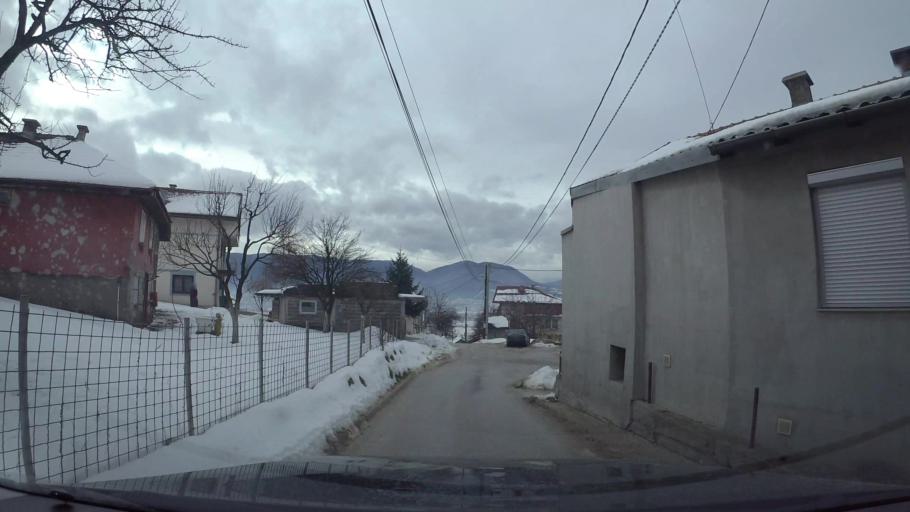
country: BA
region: Federation of Bosnia and Herzegovina
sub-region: Kanton Sarajevo
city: Sarajevo
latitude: 43.8642
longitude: 18.3299
